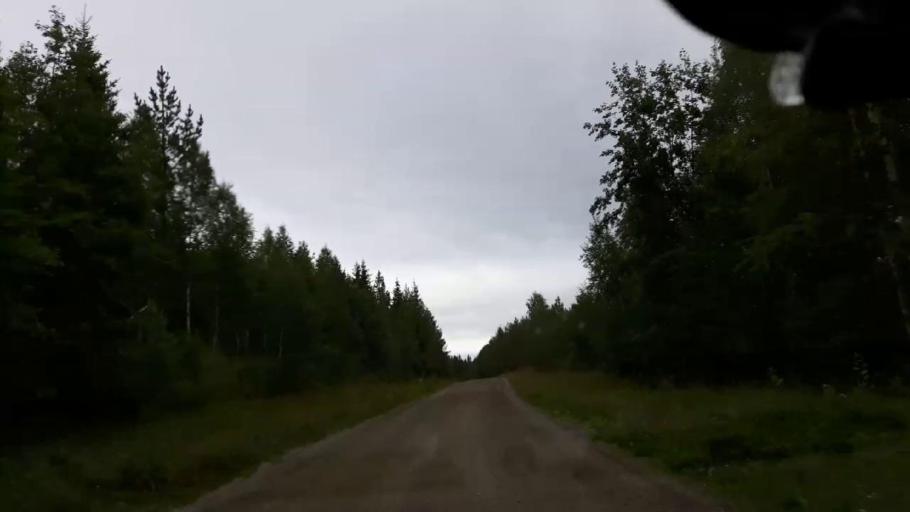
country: SE
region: Jaemtland
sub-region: Braecke Kommun
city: Braecke
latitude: 62.9307
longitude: 15.4882
